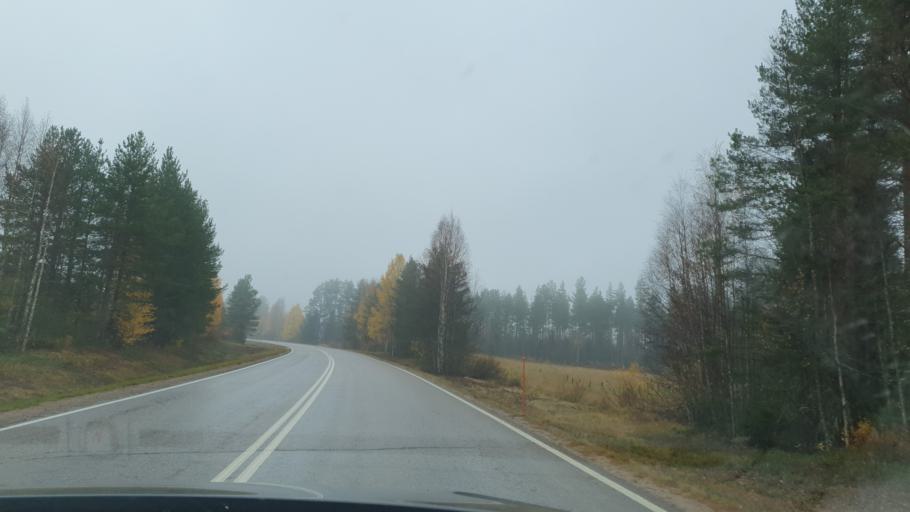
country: FI
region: Lapland
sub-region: Rovaniemi
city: Rovaniemi
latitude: 66.8202
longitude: 25.3955
